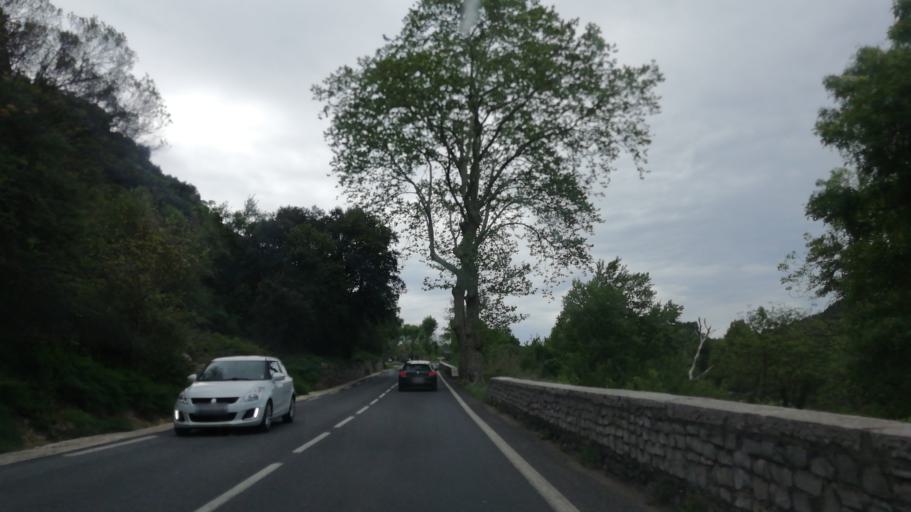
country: FR
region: Languedoc-Roussillon
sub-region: Departement de l'Herault
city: Saint-Bauzille-de-Putois
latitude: 43.9082
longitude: 3.7378
